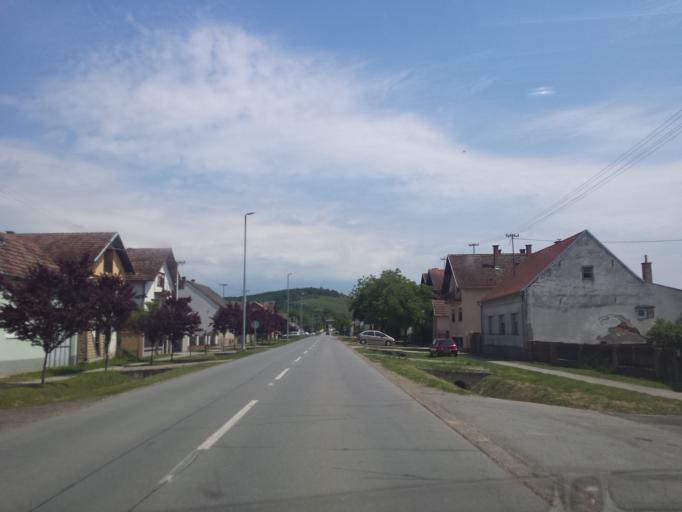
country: HR
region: Brodsko-Posavska
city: Oriovac
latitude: 45.1667
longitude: 17.7975
